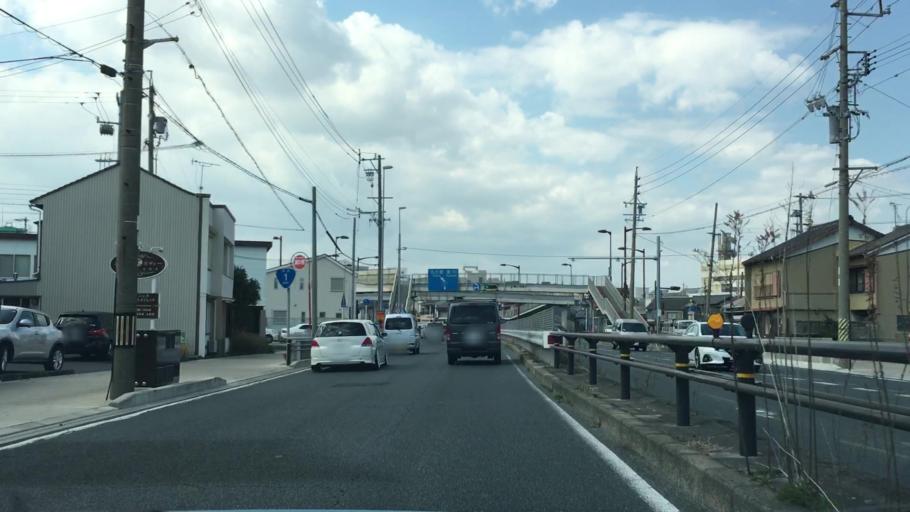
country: JP
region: Aichi
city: Toyohashi
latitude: 34.7652
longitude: 137.4010
